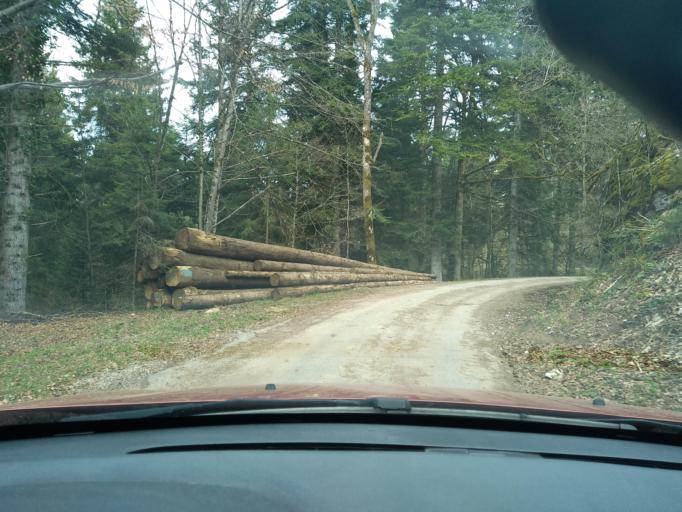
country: FR
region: Franche-Comte
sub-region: Departement du Jura
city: Moirans-en-Montagne
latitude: 46.4745
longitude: 5.7591
